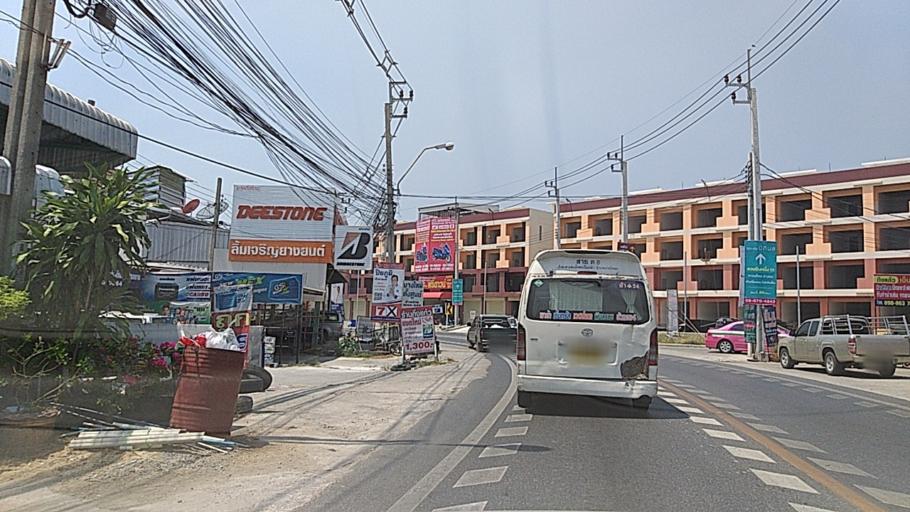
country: TH
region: Nonthaburi
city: Bang Bua Thong
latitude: 13.9151
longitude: 100.4034
